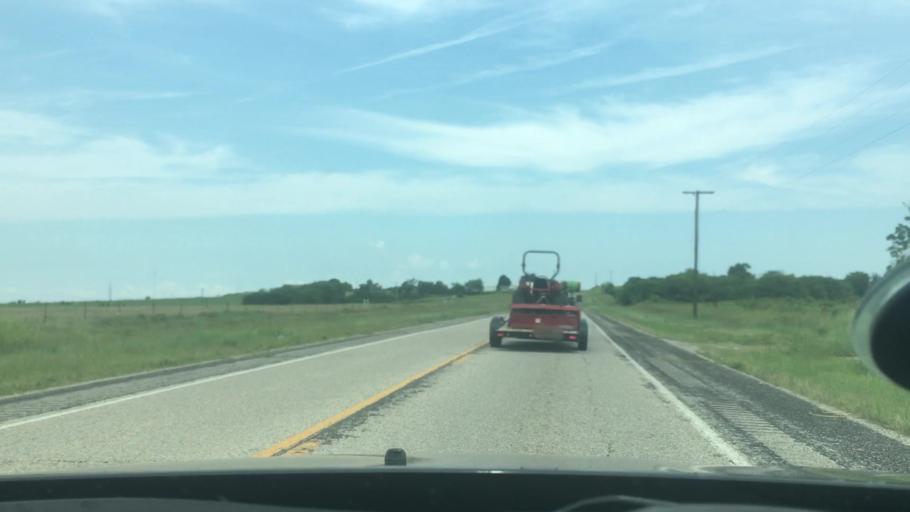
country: US
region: Oklahoma
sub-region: Seminole County
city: Seminole
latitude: 35.2717
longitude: -96.7207
